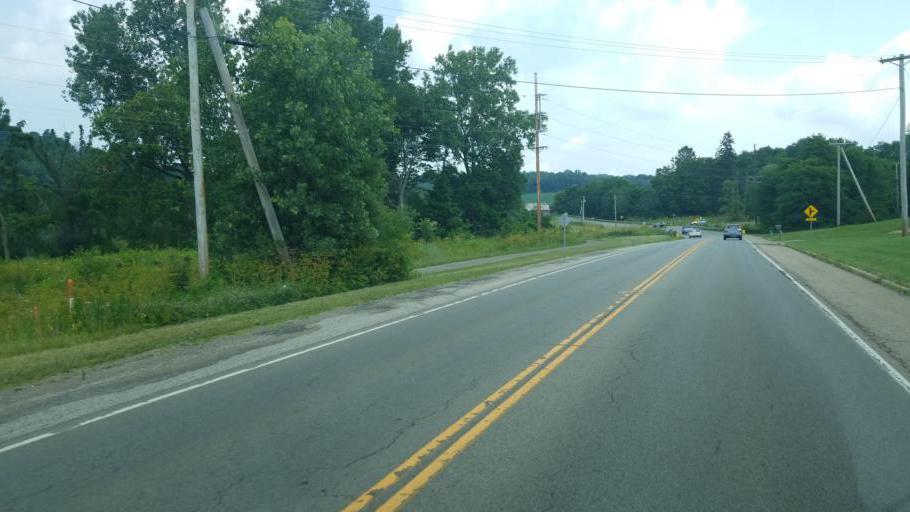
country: US
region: Ohio
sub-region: Richland County
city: Lexington
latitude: 40.7083
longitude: -82.5811
